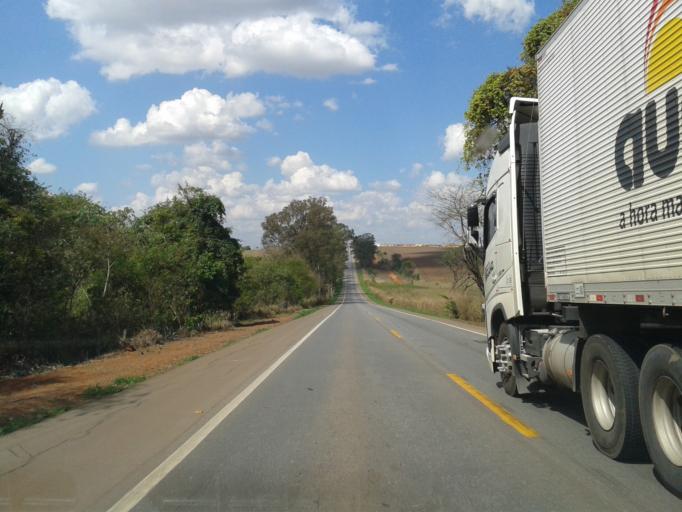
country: BR
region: Minas Gerais
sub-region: Luz
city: Luz
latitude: -19.7843
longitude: -45.7069
